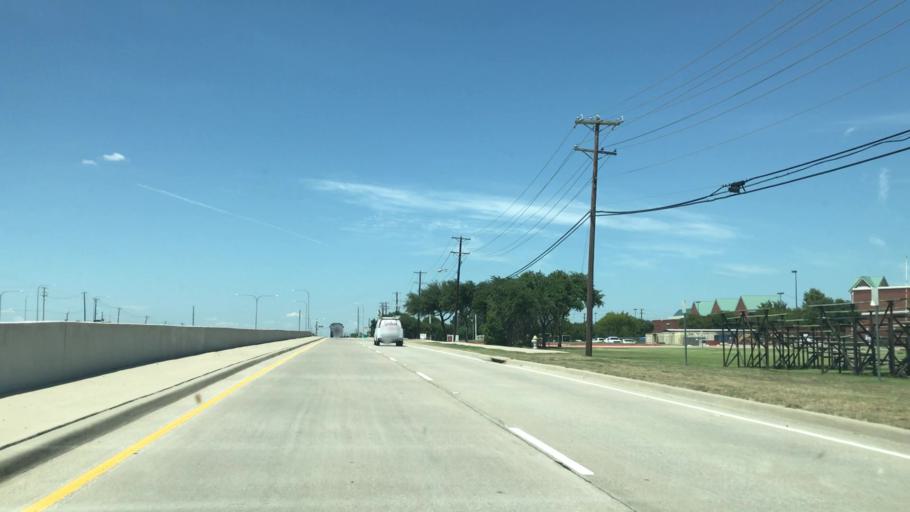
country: US
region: Texas
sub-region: Dallas County
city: Rowlett
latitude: 32.9005
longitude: -96.5555
